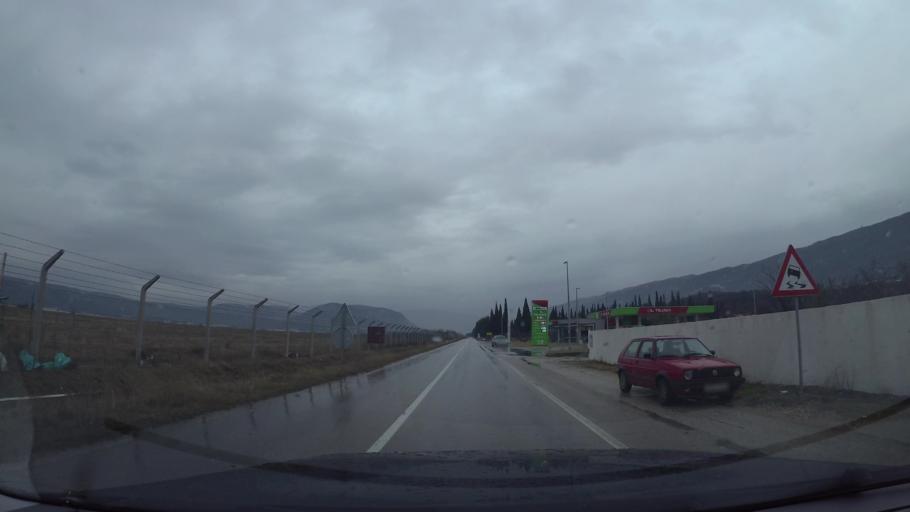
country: BA
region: Federation of Bosnia and Herzegovina
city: Rodoc
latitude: 43.2903
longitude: 17.8473
